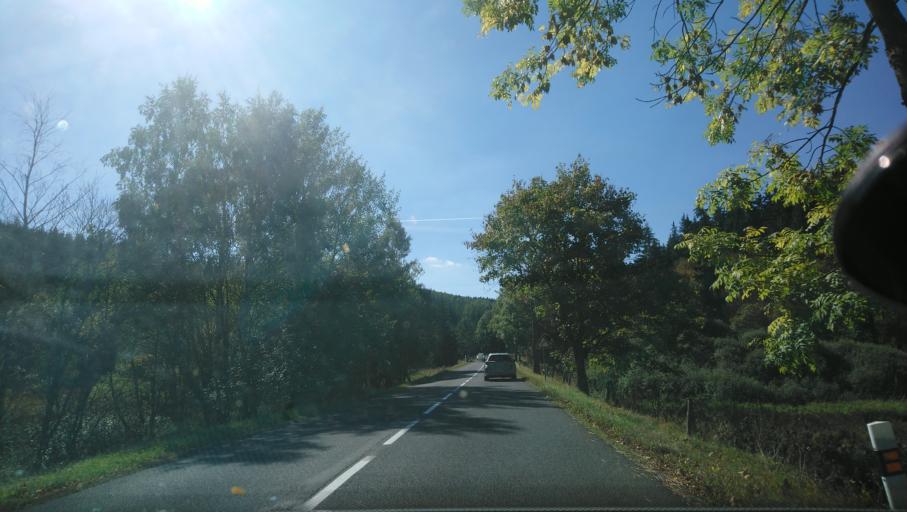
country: CZ
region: Ustecky
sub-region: Okres Chomutov
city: Kovarska
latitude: 50.4383
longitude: 13.0149
